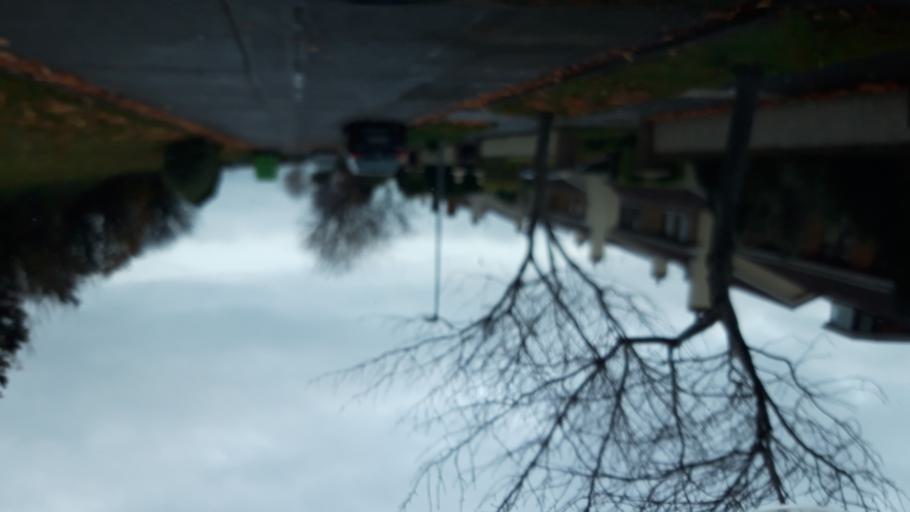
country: IE
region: Leinster
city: Malahide
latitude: 53.4451
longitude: -6.1442
